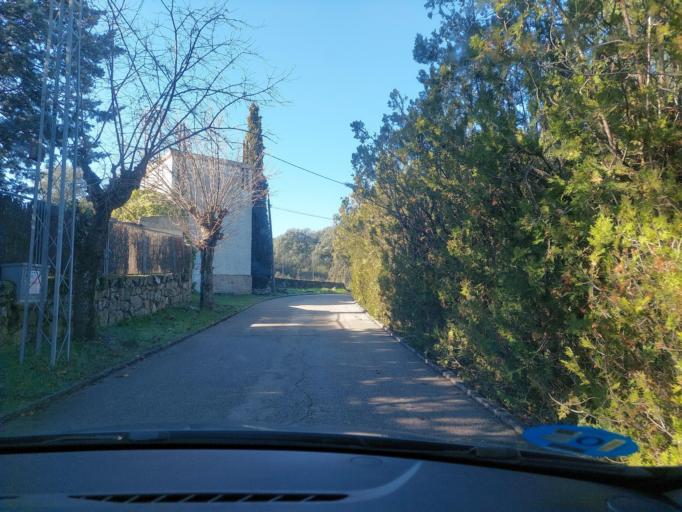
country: ES
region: Madrid
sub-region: Provincia de Madrid
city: Torrelodones
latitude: 40.5798
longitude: -3.9124
